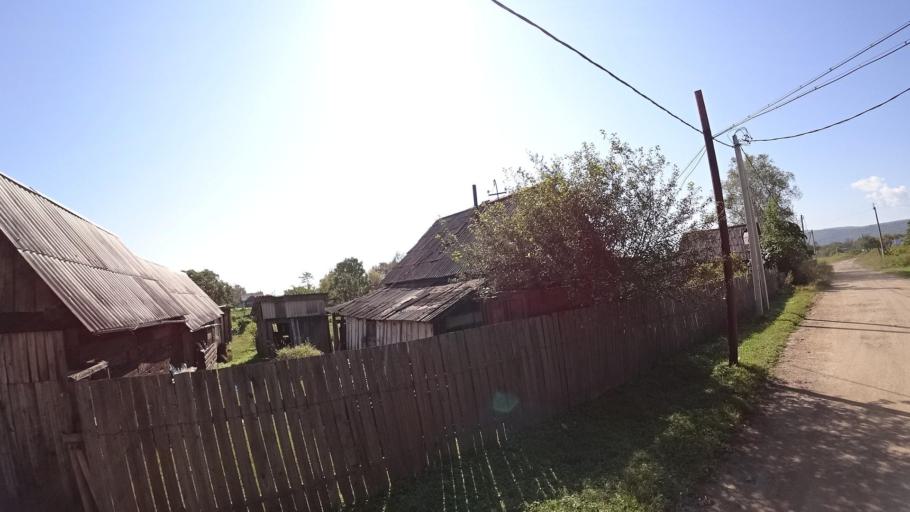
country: RU
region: Jewish Autonomous Oblast
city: Bira
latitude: 48.9948
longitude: 132.4601
